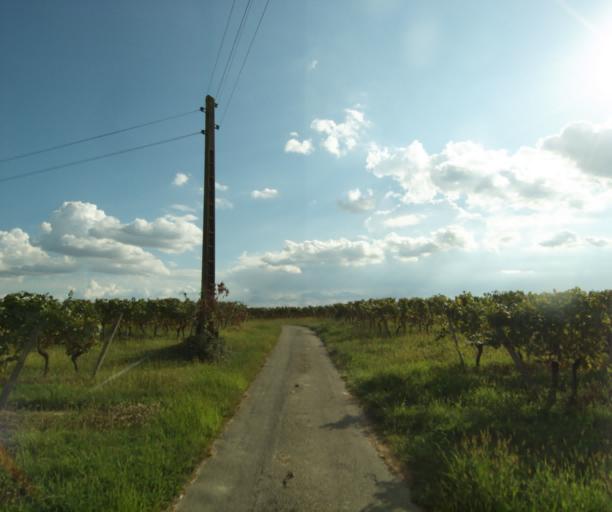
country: FR
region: Midi-Pyrenees
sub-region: Departement du Gers
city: Cazaubon
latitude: 43.8797
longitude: -0.0601
